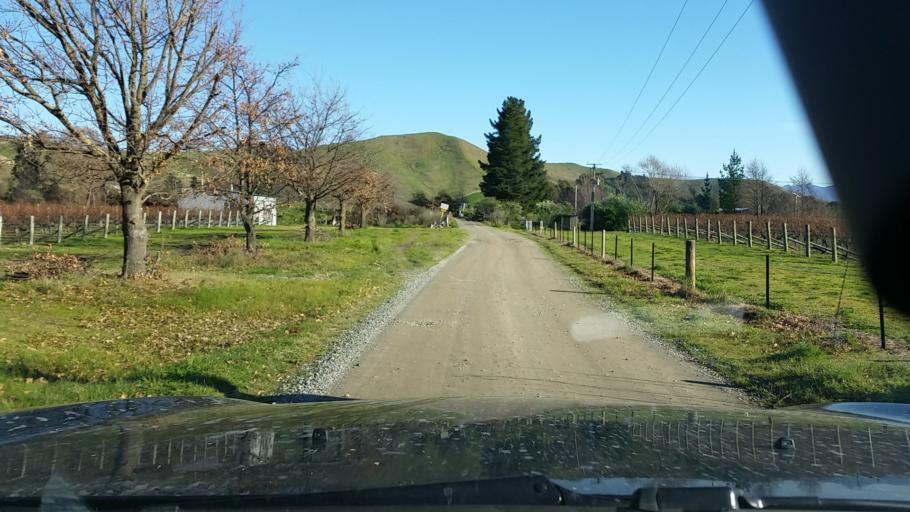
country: NZ
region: Marlborough
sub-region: Marlborough District
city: Blenheim
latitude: -41.5625
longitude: 173.9294
